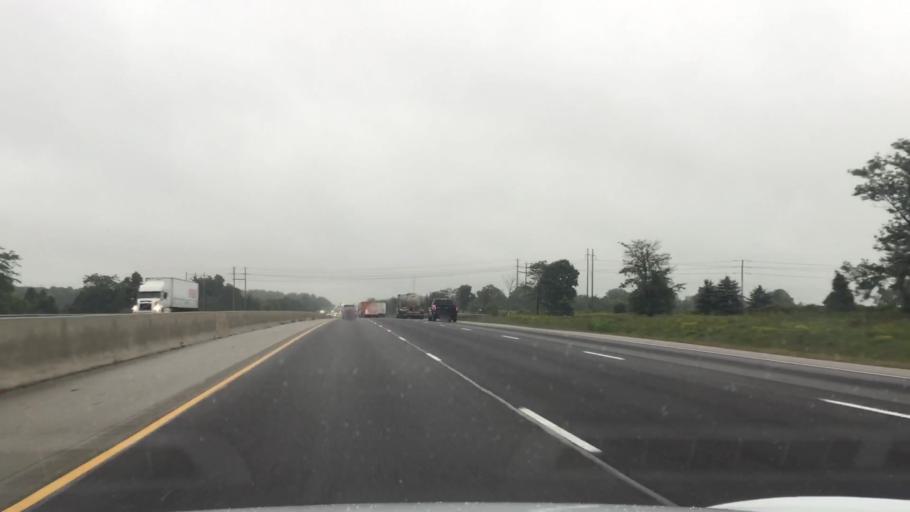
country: CA
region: Ontario
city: Kitchener
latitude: 43.2769
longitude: -80.5242
